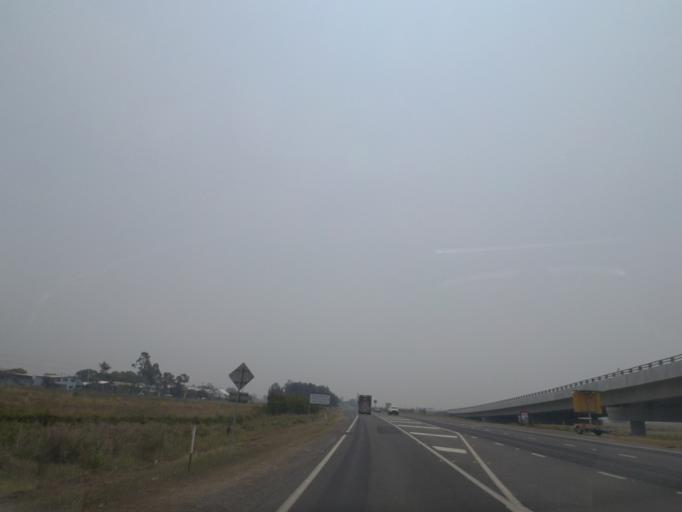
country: AU
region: New South Wales
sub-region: Clarence Valley
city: Maclean
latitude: -29.4245
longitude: 153.2412
